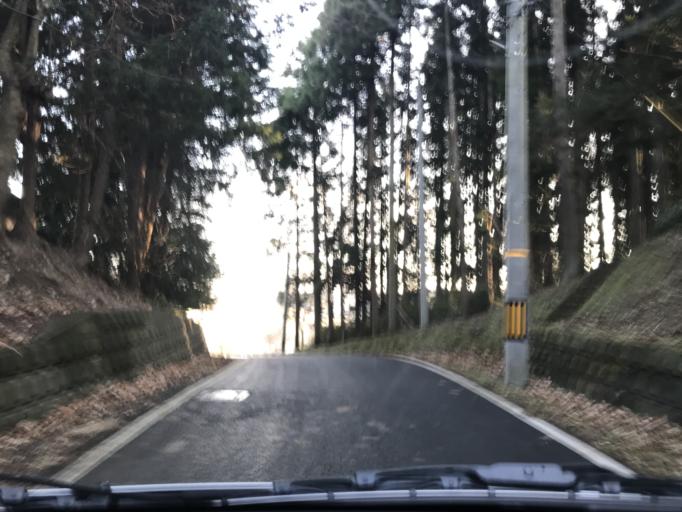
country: JP
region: Miyagi
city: Wakuya
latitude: 38.6850
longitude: 141.1123
